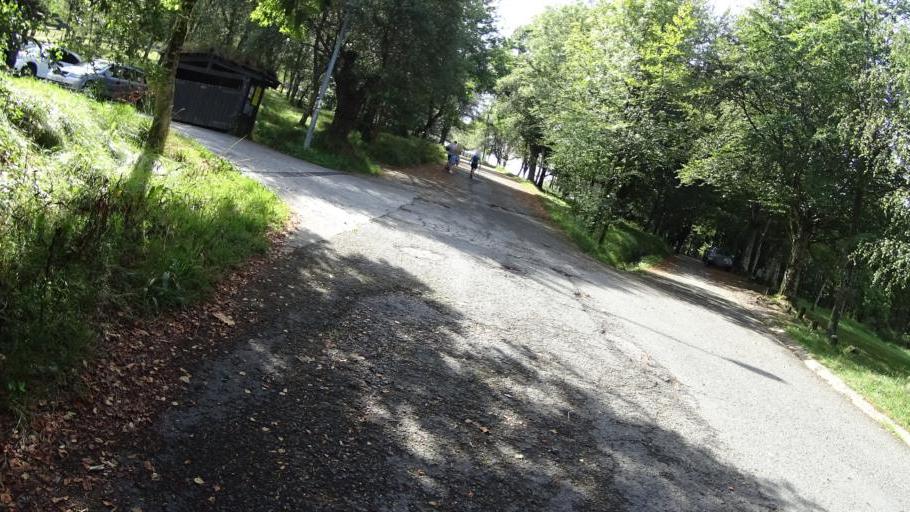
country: ES
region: Basque Country
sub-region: Bizkaia
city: Manaria
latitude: 43.0996
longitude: -2.6426
